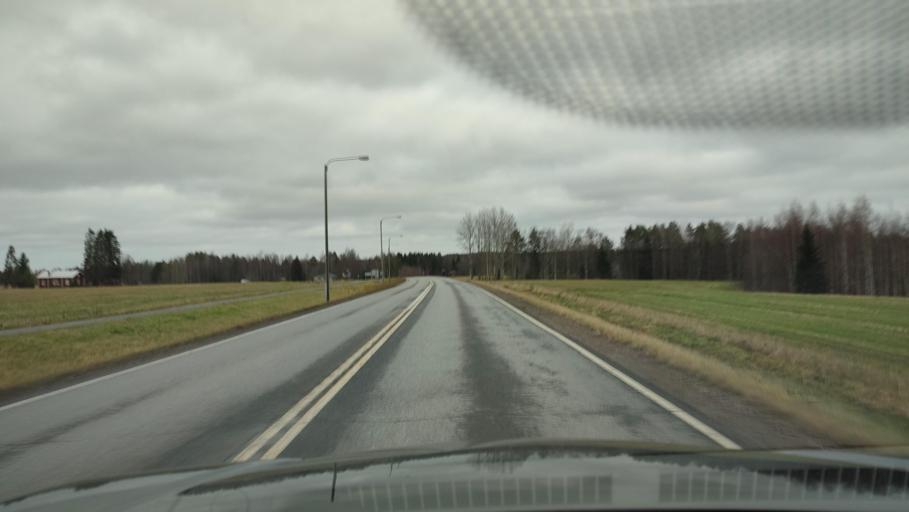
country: FI
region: Southern Ostrobothnia
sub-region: Seinaejoki
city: Kurikka
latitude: 62.5868
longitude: 22.4064
